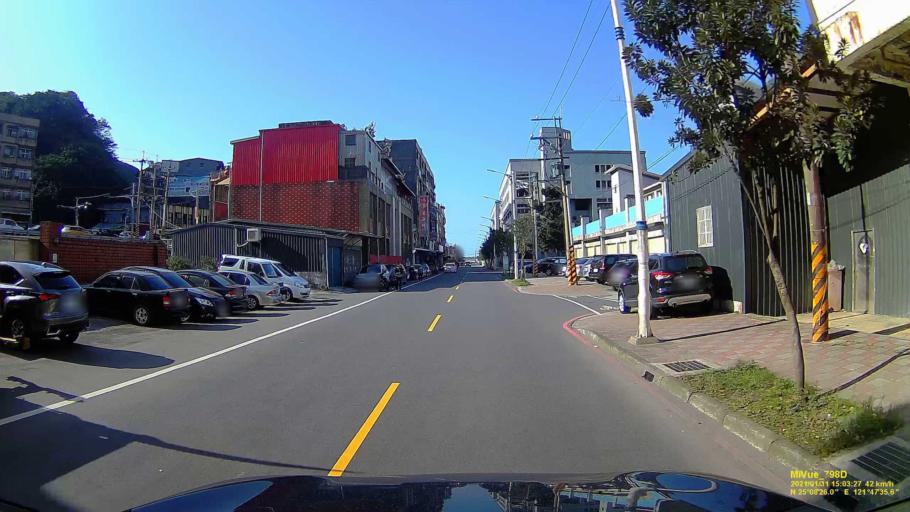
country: TW
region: Taiwan
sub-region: Keelung
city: Keelung
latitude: 25.1406
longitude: 121.7932
